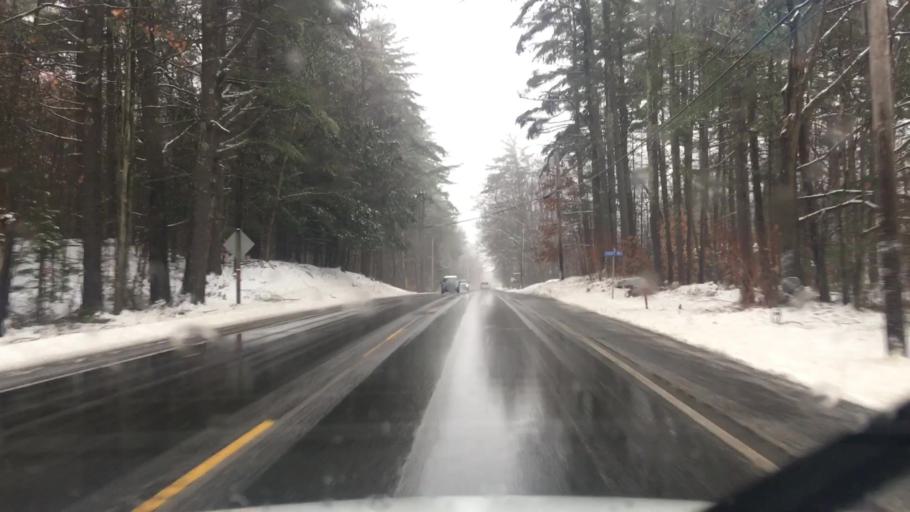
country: US
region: Maine
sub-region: York County
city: Buxton
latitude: 43.7198
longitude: -70.5259
